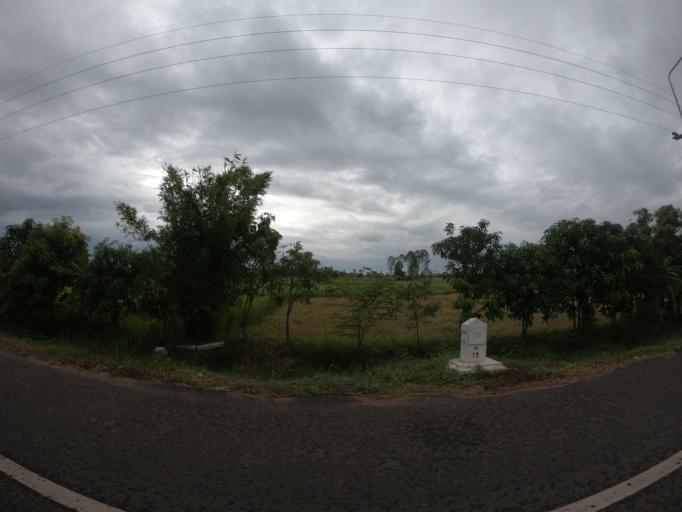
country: TH
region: Roi Et
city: Thawat Buri
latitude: 16.0971
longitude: 103.7925
